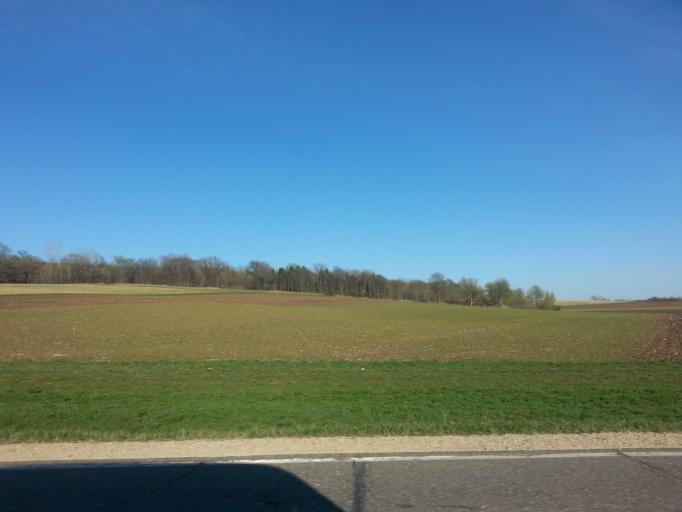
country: US
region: Minnesota
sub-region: Dakota County
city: Lakeville
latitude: 44.6211
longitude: -93.2625
